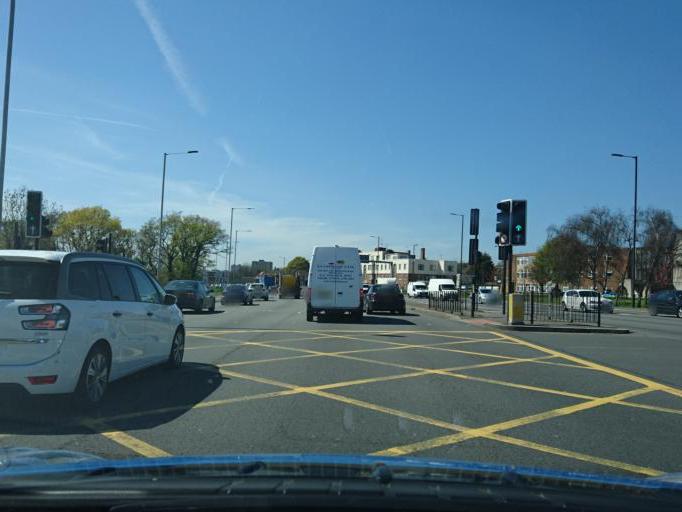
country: GB
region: England
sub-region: Greater London
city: Hendon
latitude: 51.5897
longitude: -0.1999
